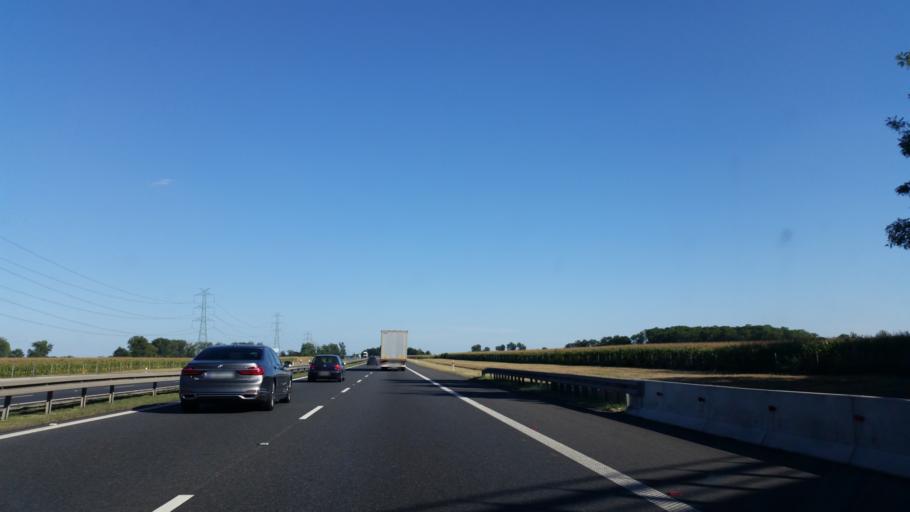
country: PL
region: Lower Silesian Voivodeship
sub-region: Powiat olawski
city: Wierzbno
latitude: 50.9193
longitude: 17.1367
